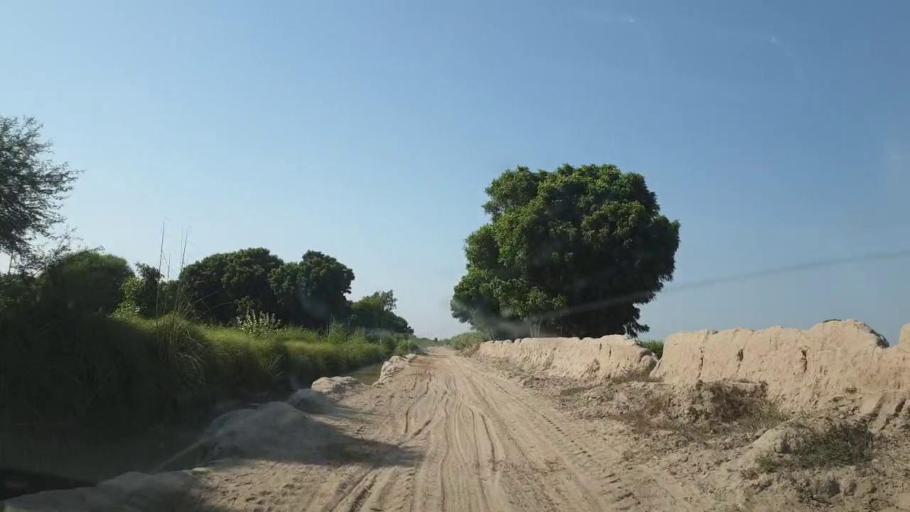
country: PK
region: Sindh
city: Tando Jam
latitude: 25.3156
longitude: 68.6059
